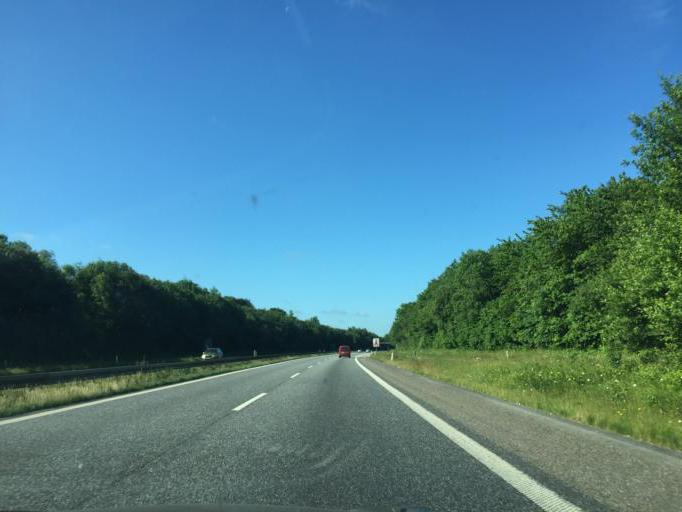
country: DK
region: South Denmark
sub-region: Haderslev Kommune
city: Haderslev
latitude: 55.2438
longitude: 9.3996
